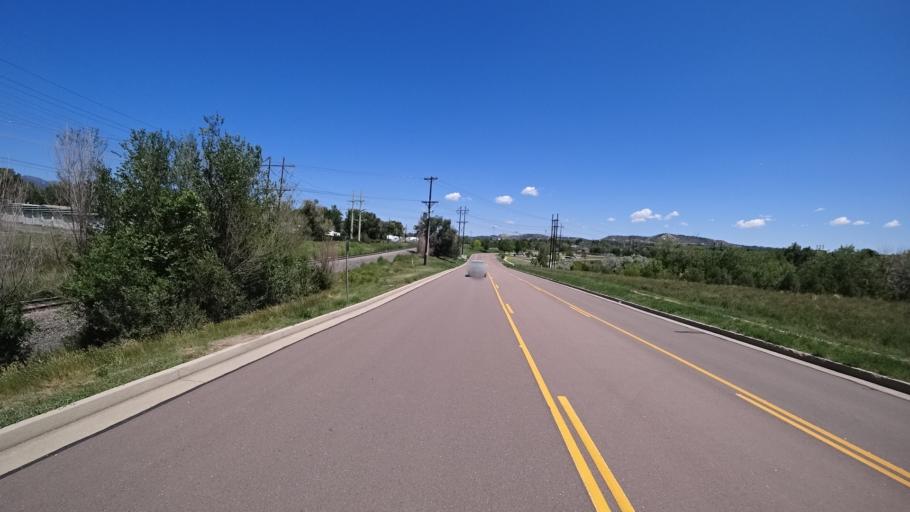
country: US
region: Colorado
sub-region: El Paso County
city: Colorado Springs
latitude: 38.8773
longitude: -104.8316
